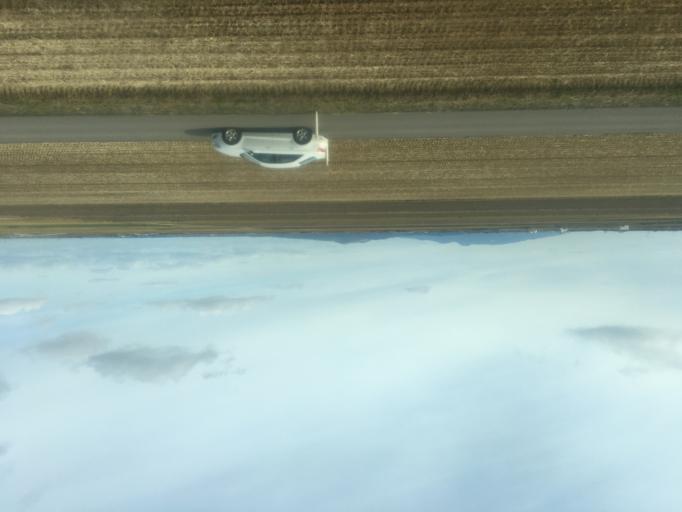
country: JP
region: Akita
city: Tenno
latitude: 39.8920
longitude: 140.0706
